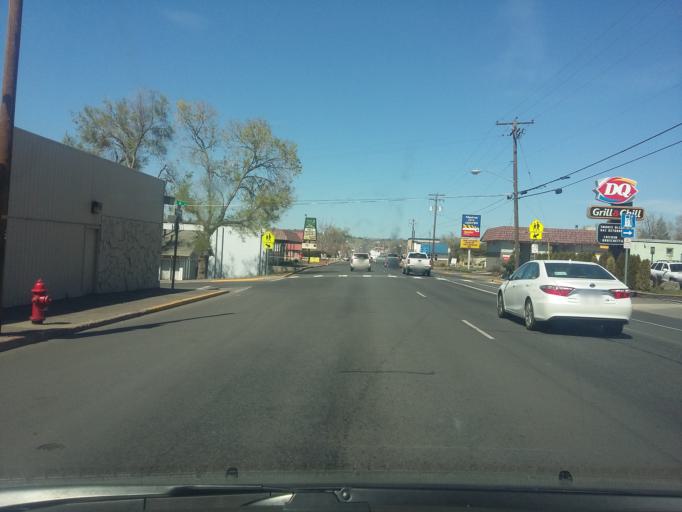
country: US
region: Oregon
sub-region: Jefferson County
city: Madras
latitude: 44.6287
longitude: -121.1296
